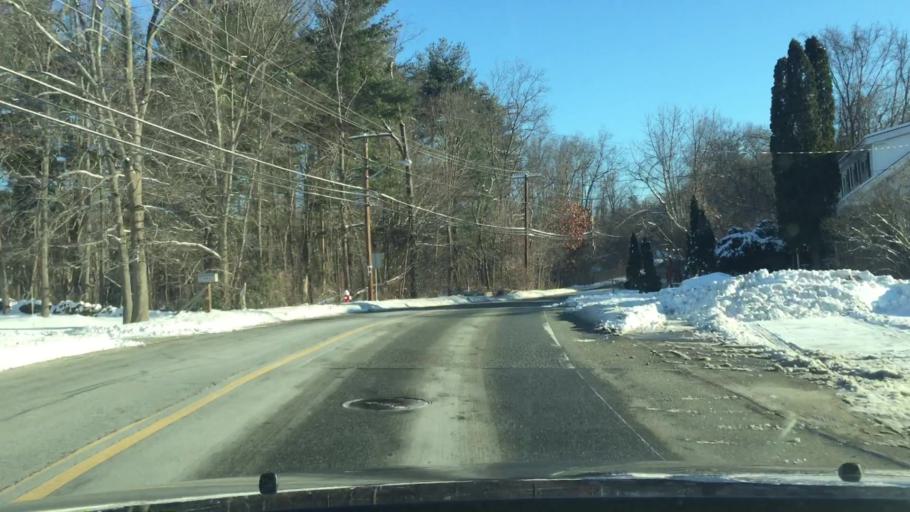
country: US
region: Massachusetts
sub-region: Middlesex County
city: Dracut
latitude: 42.6827
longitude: -71.2847
